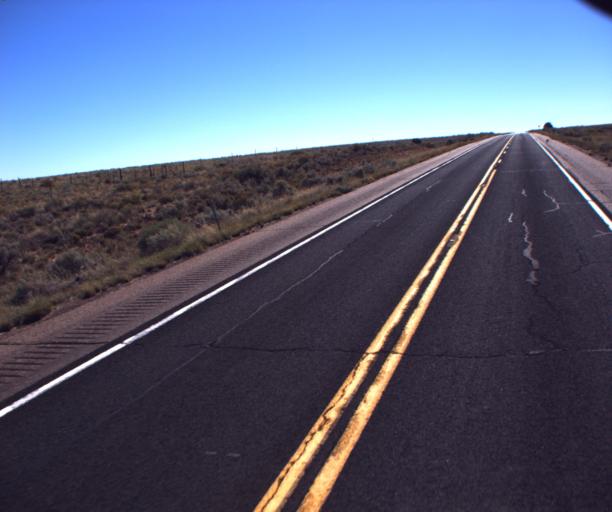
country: US
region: Arizona
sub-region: Navajo County
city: Snowflake
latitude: 34.7138
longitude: -109.7660
